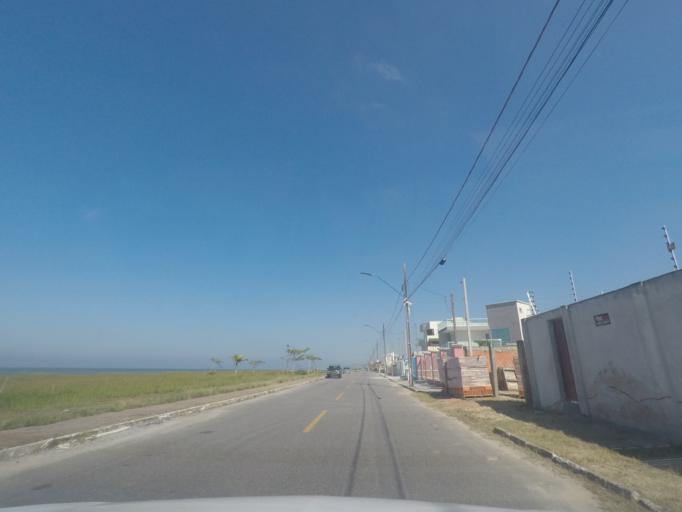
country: BR
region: Parana
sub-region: Pontal Do Parana
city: Pontal do Parana
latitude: -25.7423
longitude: -48.4957
